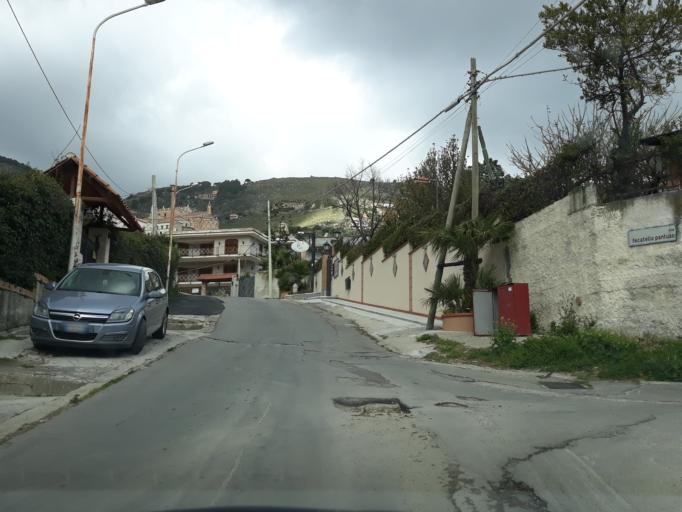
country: IT
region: Sicily
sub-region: Palermo
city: Monreale
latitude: 38.0800
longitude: 13.2968
